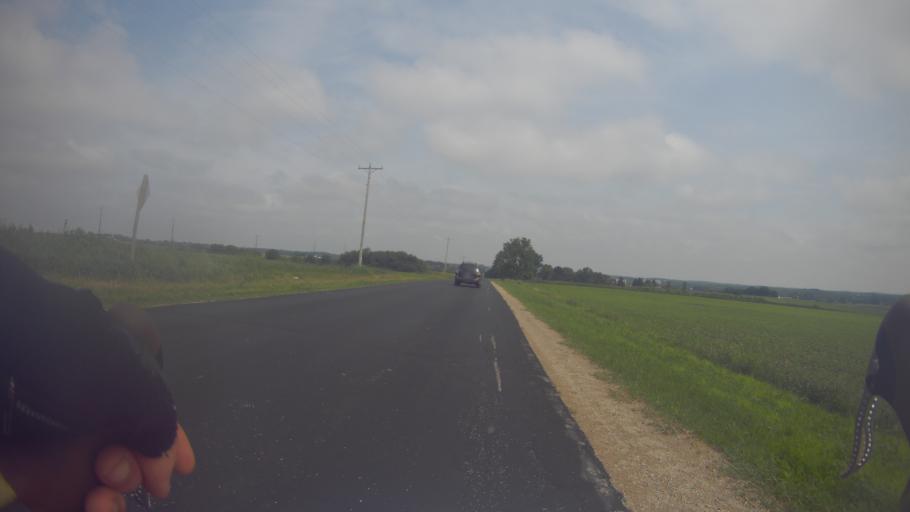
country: US
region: Wisconsin
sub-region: Rock County
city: Edgerton
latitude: 42.9082
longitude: -89.0427
